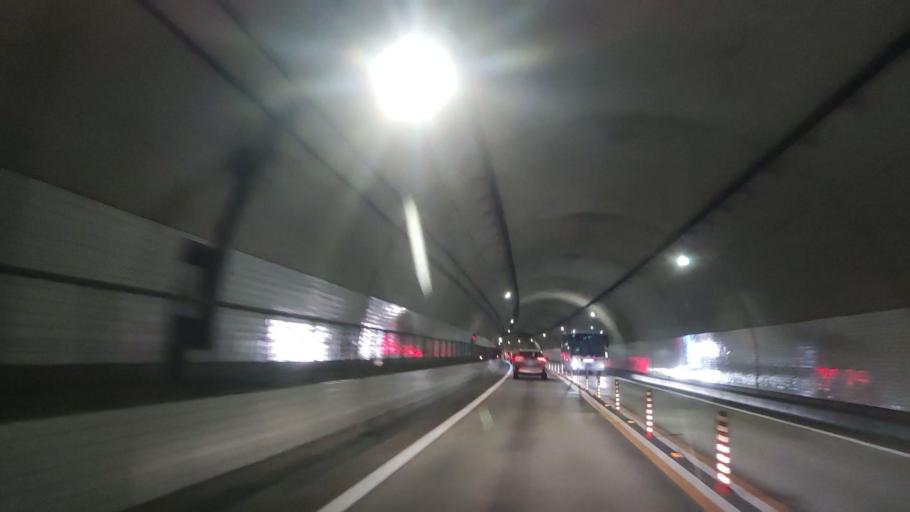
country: JP
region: Kyoto
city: Miyazu
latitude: 35.5627
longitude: 135.1216
